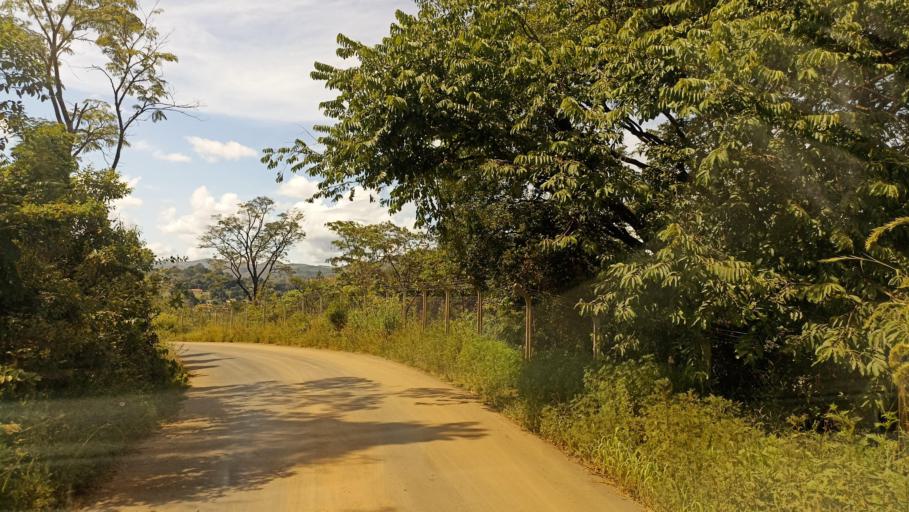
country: BR
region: Minas Gerais
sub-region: Itabirito
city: Itabirito
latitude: -20.3527
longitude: -43.7223
